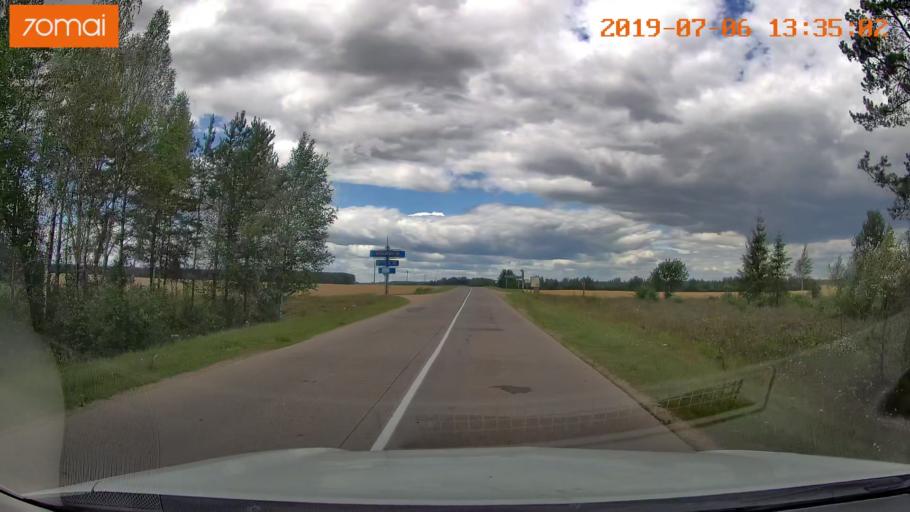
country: BY
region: Minsk
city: Enyerhyetykaw
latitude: 53.6791
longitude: 26.8877
